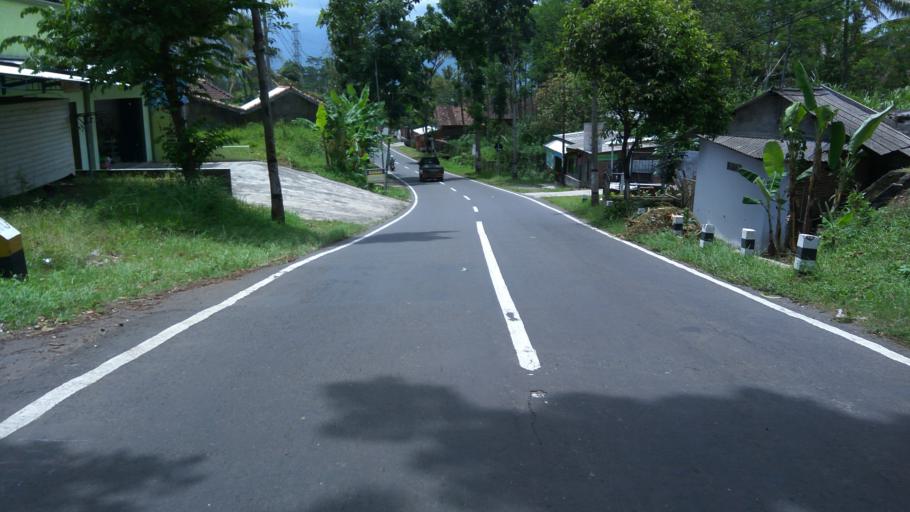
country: ID
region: Central Java
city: Ambarawa
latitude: -7.2462
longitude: 110.3985
